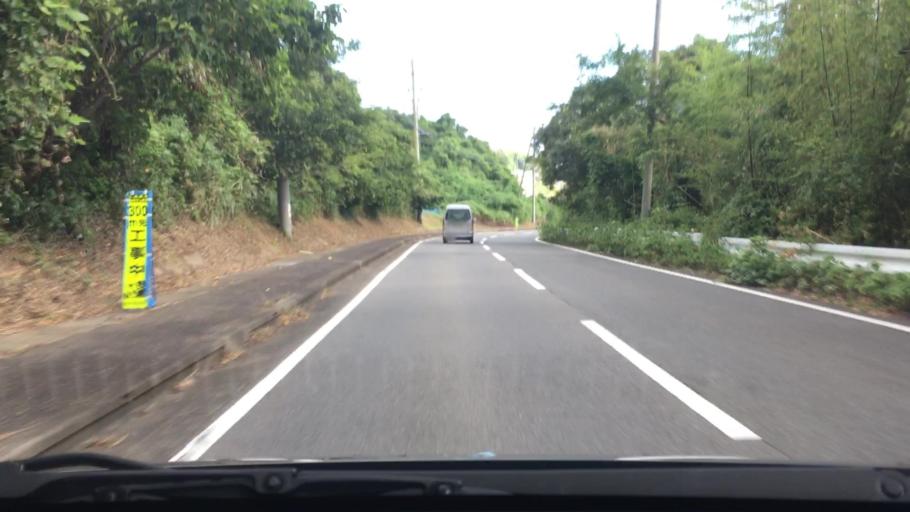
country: JP
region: Nagasaki
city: Togitsu
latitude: 32.8609
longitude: 129.6846
